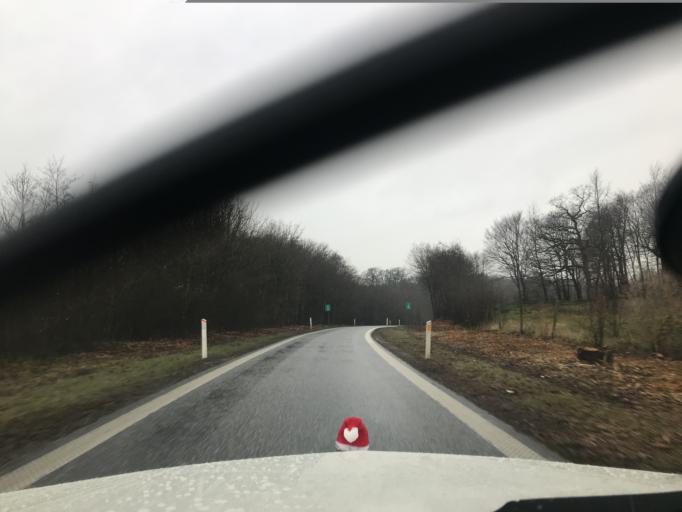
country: DK
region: South Denmark
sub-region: Aabenraa Kommune
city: Aabenraa
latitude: 55.0010
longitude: 9.3704
